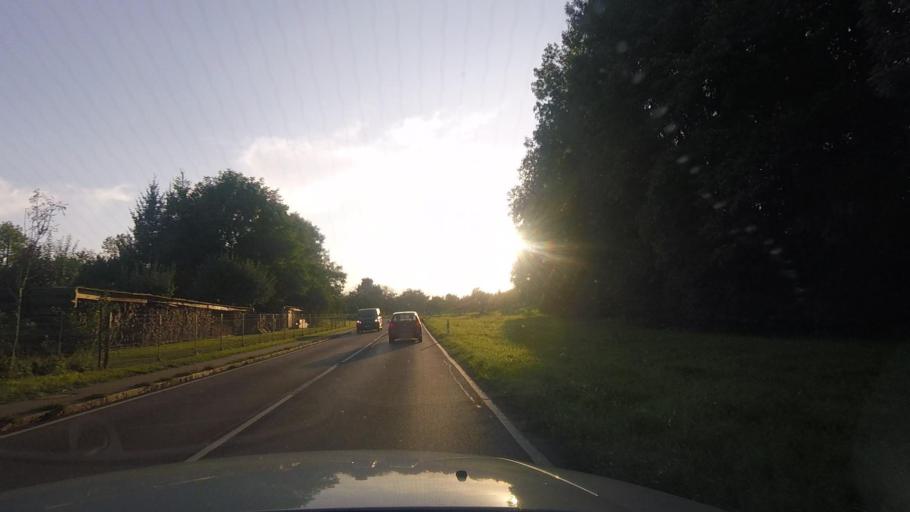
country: DE
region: Baden-Wuerttemberg
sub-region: Regierungsbezirk Stuttgart
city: Erdmannhausen
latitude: 48.9491
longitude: 9.2876
